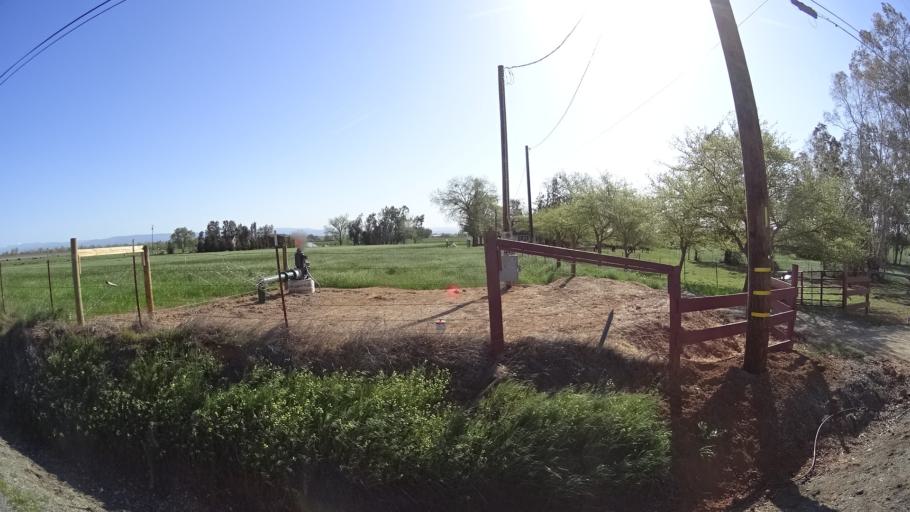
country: US
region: California
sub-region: Glenn County
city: Hamilton City
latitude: 39.7774
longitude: -122.0666
